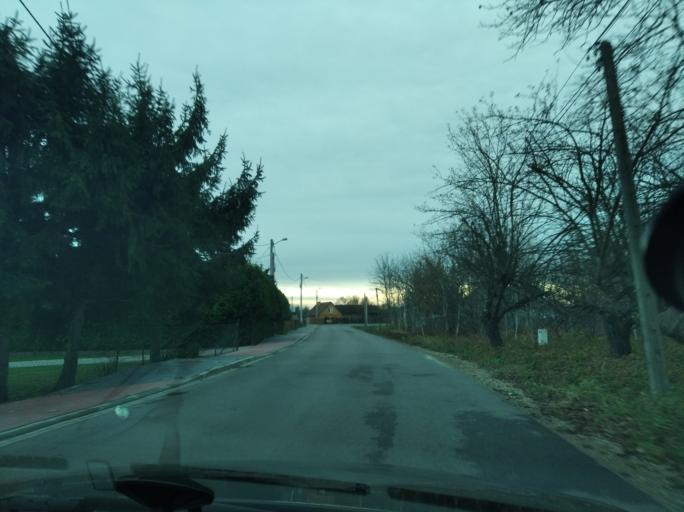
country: PL
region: Subcarpathian Voivodeship
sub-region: Powiat lancucki
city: Czarna
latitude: 50.0973
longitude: 22.1982
